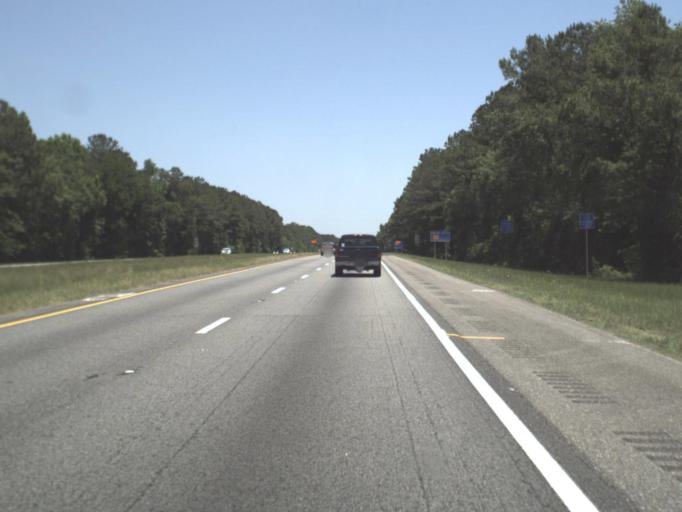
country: US
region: Florida
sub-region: Jefferson County
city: Monticello
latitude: 30.4837
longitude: -84.0413
